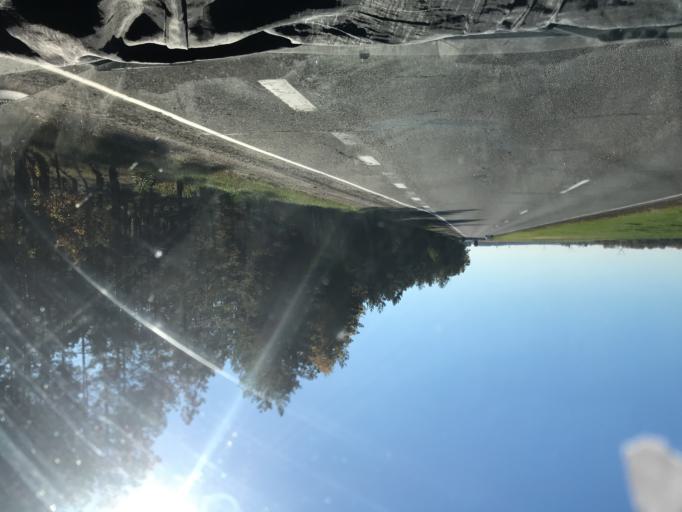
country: BY
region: Gomel
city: Parychy
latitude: 52.8686
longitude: 29.3234
